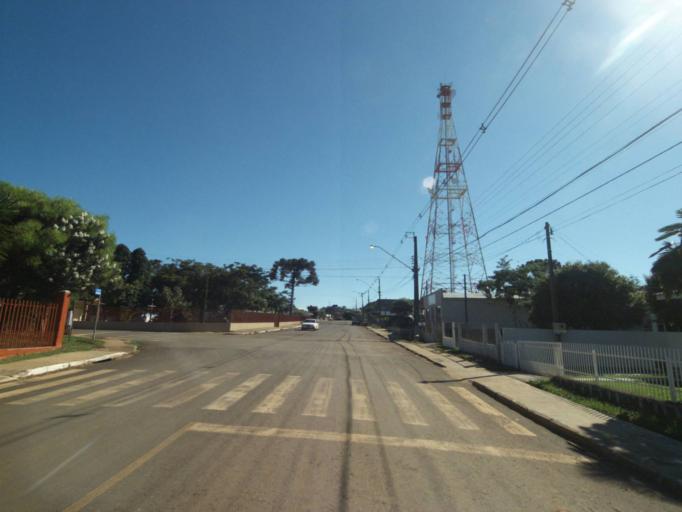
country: BR
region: Parana
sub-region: Pinhao
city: Pinhao
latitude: -25.8400
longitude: -52.0281
